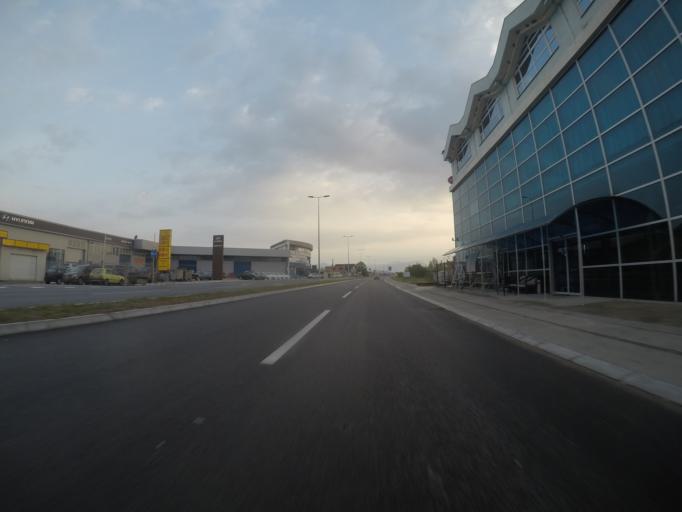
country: ME
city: Mojanovici
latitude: 42.3567
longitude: 19.2233
